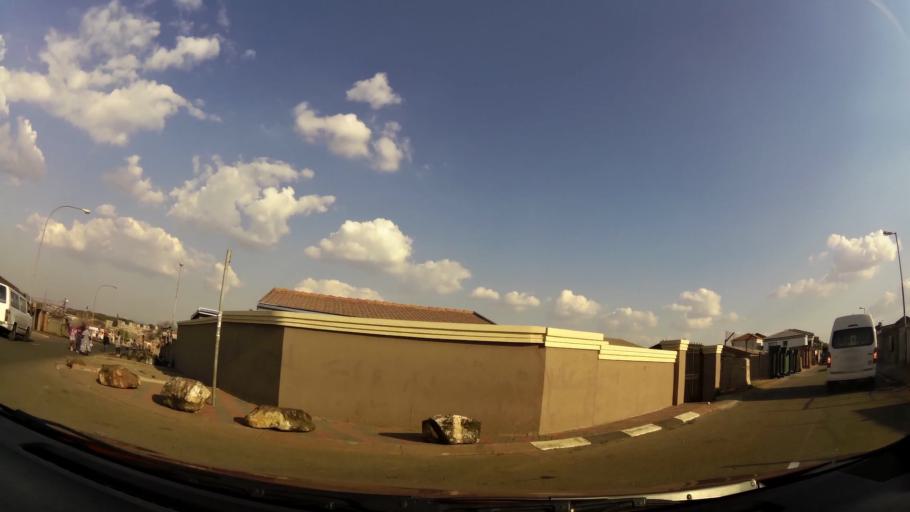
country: ZA
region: Gauteng
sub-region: City of Johannesburg Metropolitan Municipality
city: Soweto
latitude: -26.2356
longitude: 27.8610
